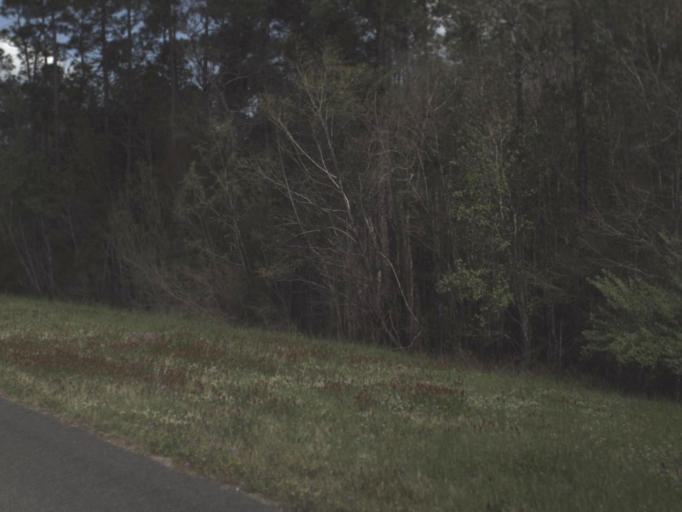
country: US
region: Florida
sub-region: Santa Rosa County
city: Point Baker
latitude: 30.8813
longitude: -86.9558
